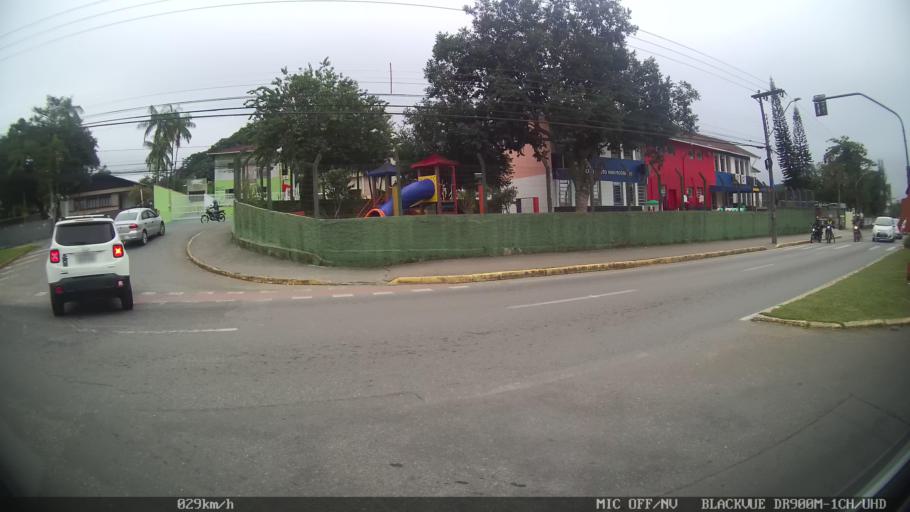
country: BR
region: Santa Catarina
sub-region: Joinville
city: Joinville
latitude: -26.2710
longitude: -48.8265
